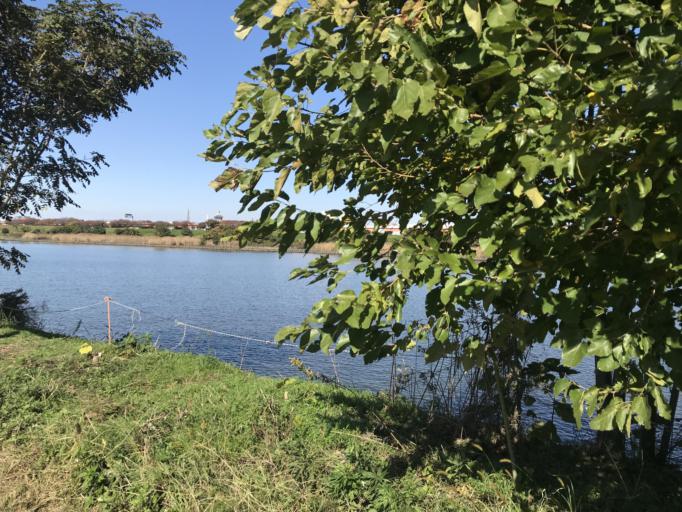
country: JP
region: Saitama
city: Kawaguchi
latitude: 35.7696
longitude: 139.7558
